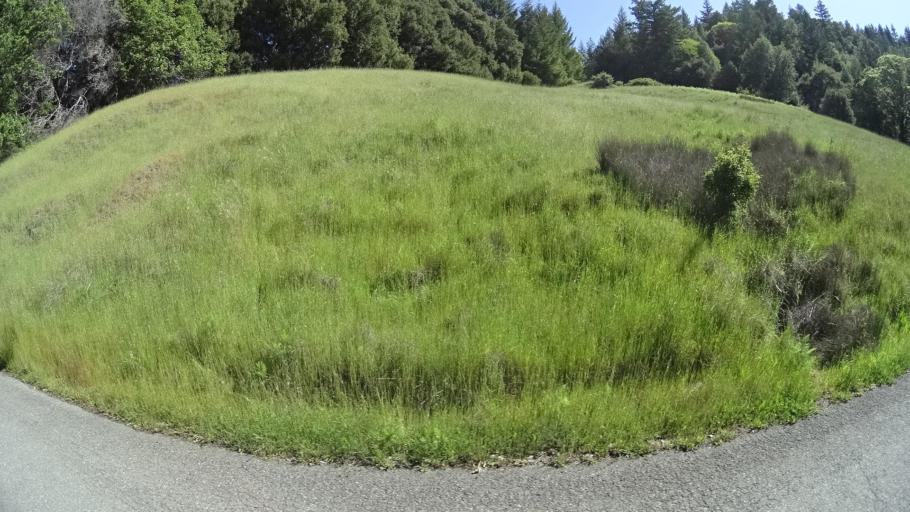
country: US
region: California
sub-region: Humboldt County
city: Rio Dell
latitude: 40.2174
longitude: -124.1120
